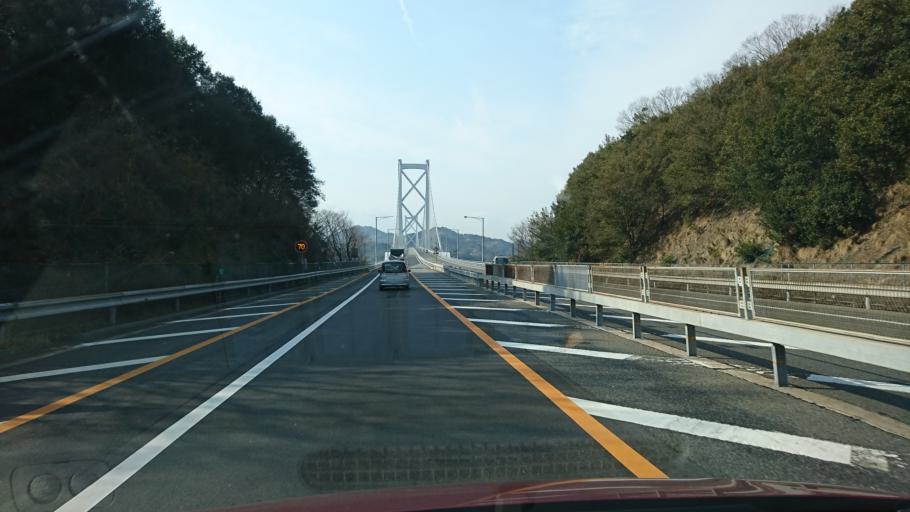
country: JP
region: Hiroshima
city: Onomichi
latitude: 34.3609
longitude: 133.1892
